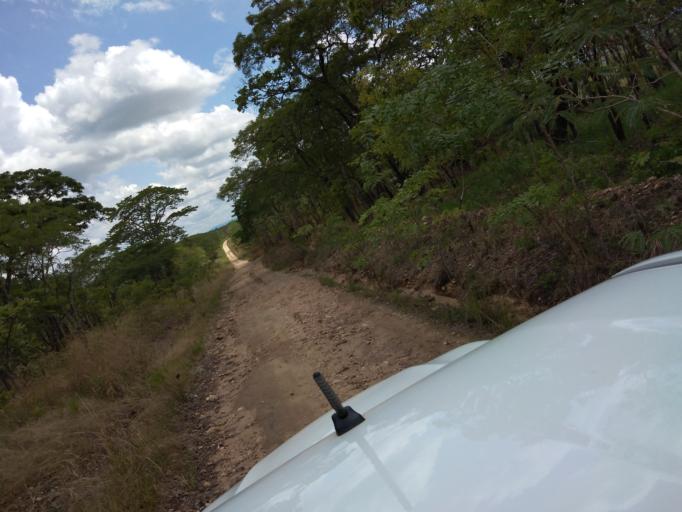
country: ZM
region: Central
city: Mkushi
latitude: -14.0616
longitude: 29.9602
